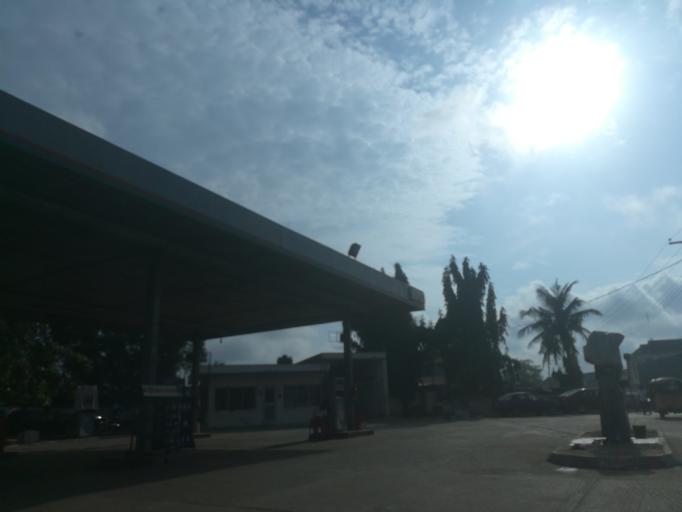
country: NG
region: Lagos
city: Agege
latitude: 6.6264
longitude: 3.3095
